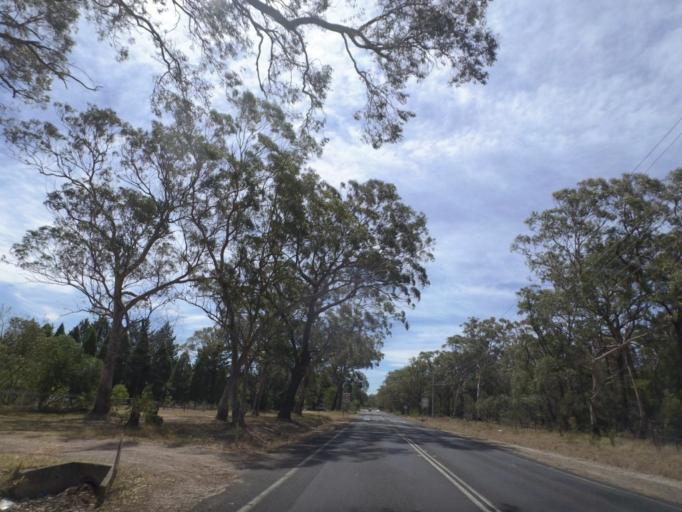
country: AU
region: New South Wales
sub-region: Wollondilly
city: Buxton
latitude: -34.3078
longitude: 150.5926
